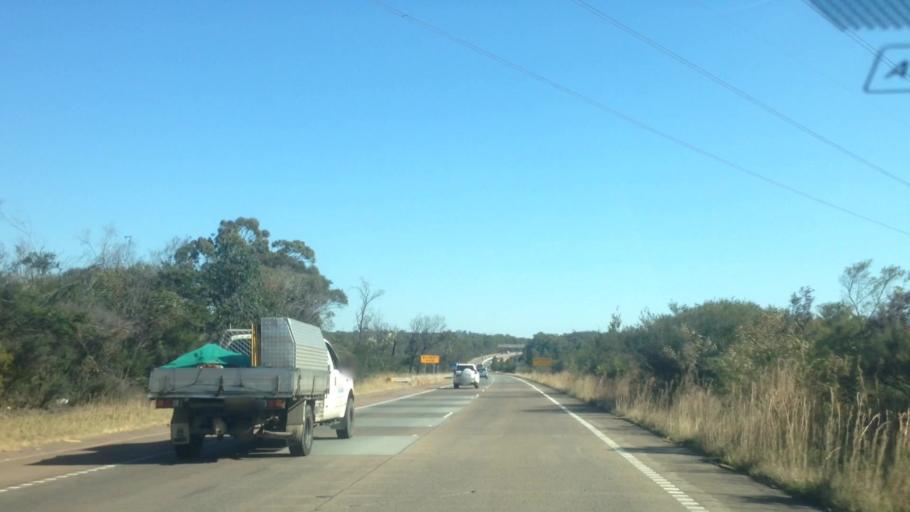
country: AU
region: New South Wales
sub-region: Wyong Shire
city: Jilliby
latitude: -33.2074
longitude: 151.4558
